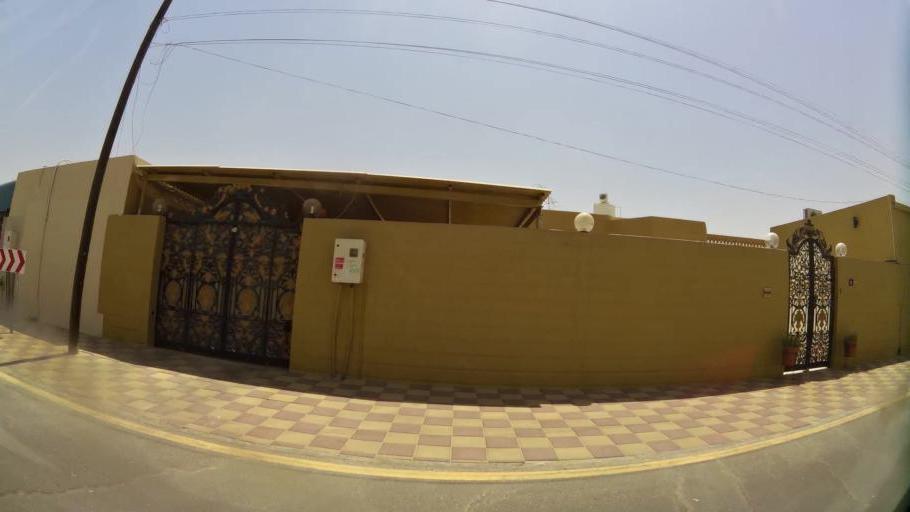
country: AE
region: Ajman
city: Ajman
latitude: 25.4026
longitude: 55.5131
